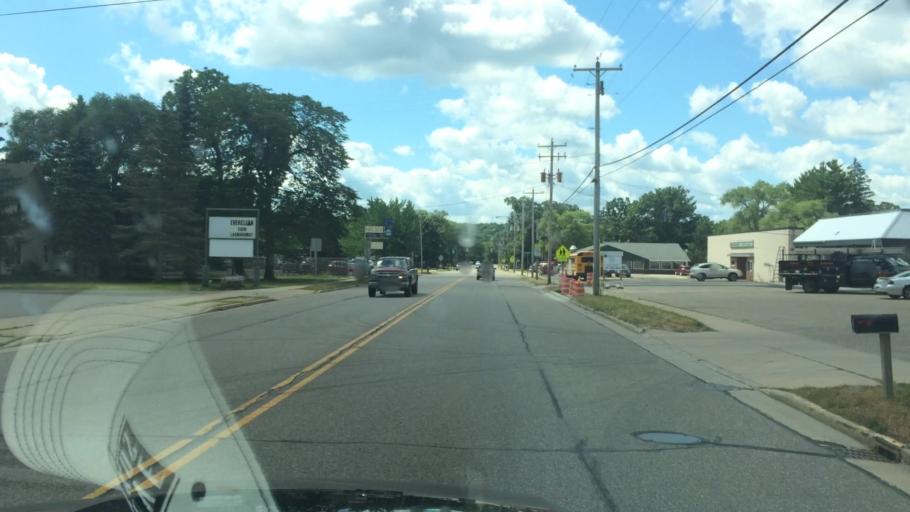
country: US
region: Wisconsin
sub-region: Waupaca County
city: Waupaca
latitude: 44.3502
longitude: -89.0722
